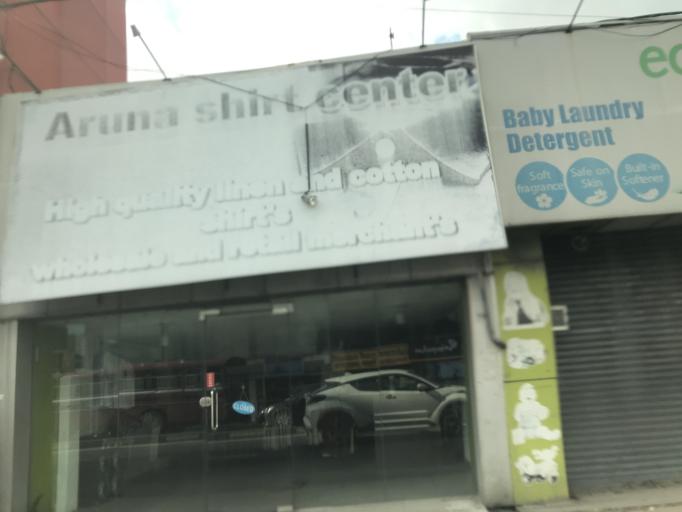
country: LK
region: Western
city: Kelaniya
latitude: 6.9789
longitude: 79.9278
